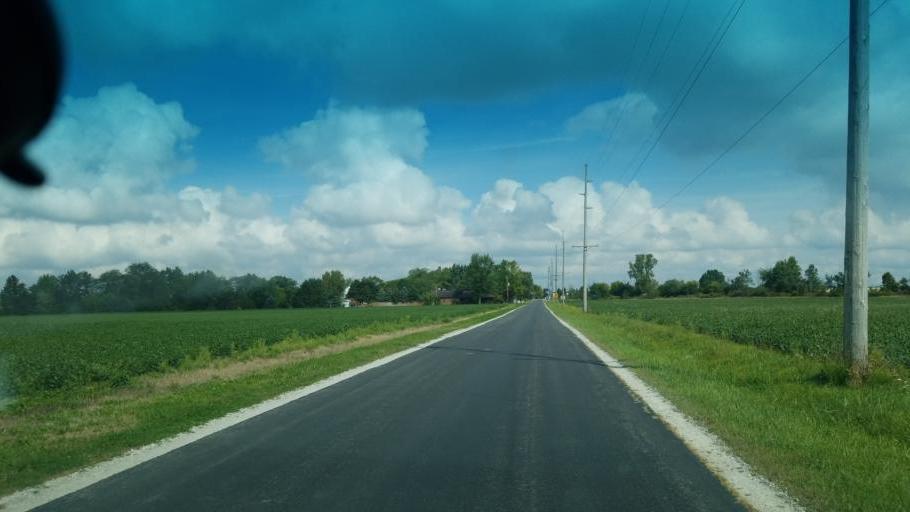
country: US
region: Ohio
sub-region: Wyandot County
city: Carey
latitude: 40.9378
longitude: -83.3674
